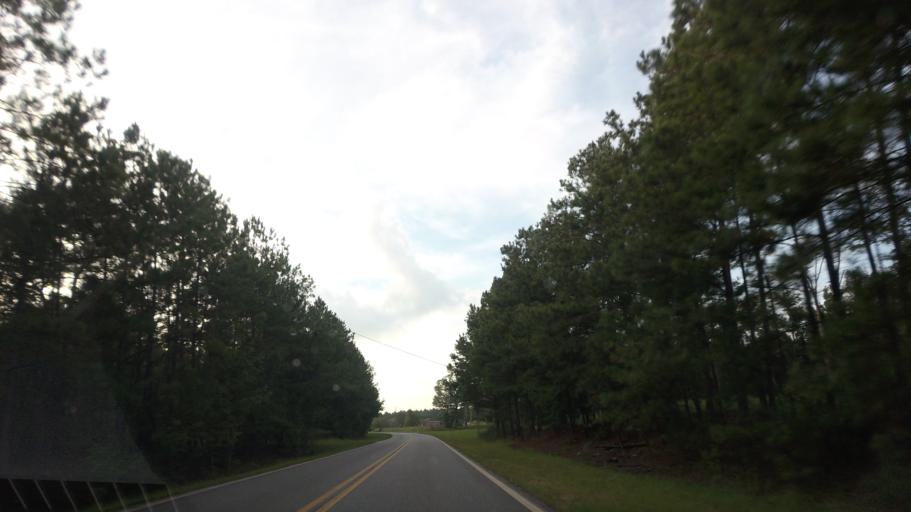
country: US
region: Georgia
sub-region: Wilkinson County
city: Gordon
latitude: 32.8644
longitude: -83.4640
